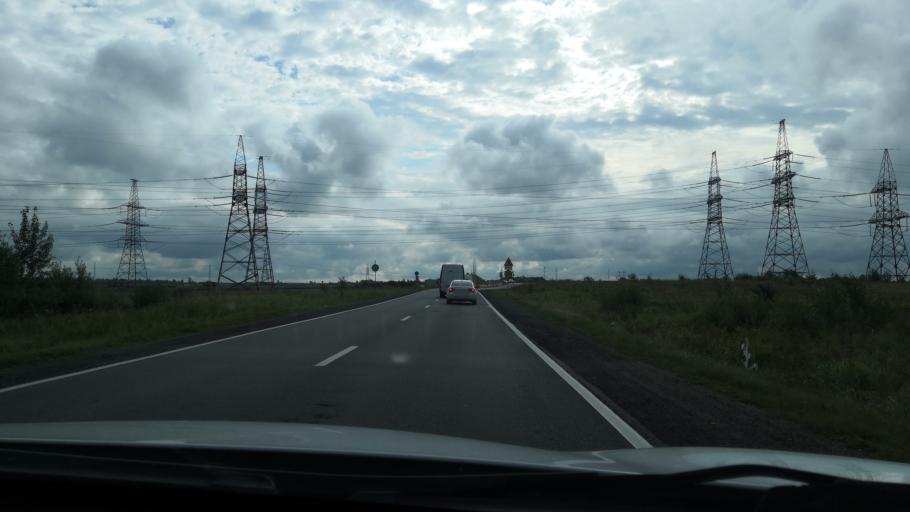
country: RU
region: Leningrad
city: Fedorovskoye
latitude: 59.7072
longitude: 30.5335
